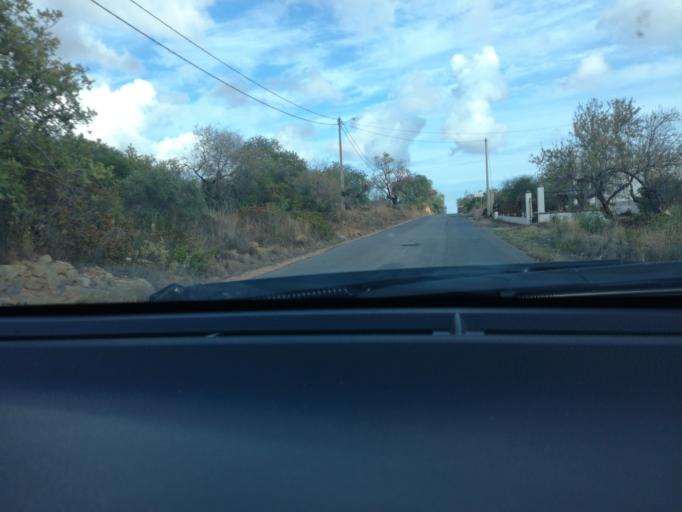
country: PT
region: Faro
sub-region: Olhao
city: Olhao
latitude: 37.0844
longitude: -7.8745
